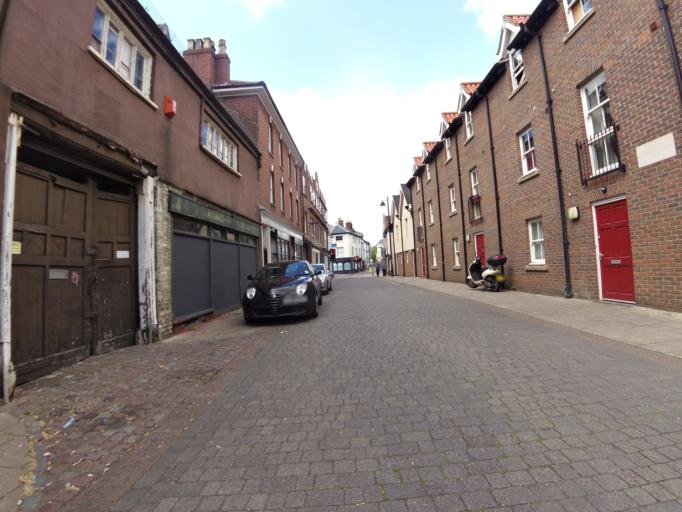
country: GB
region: England
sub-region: Norfolk
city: Norwich
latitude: 52.6275
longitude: 1.2996
